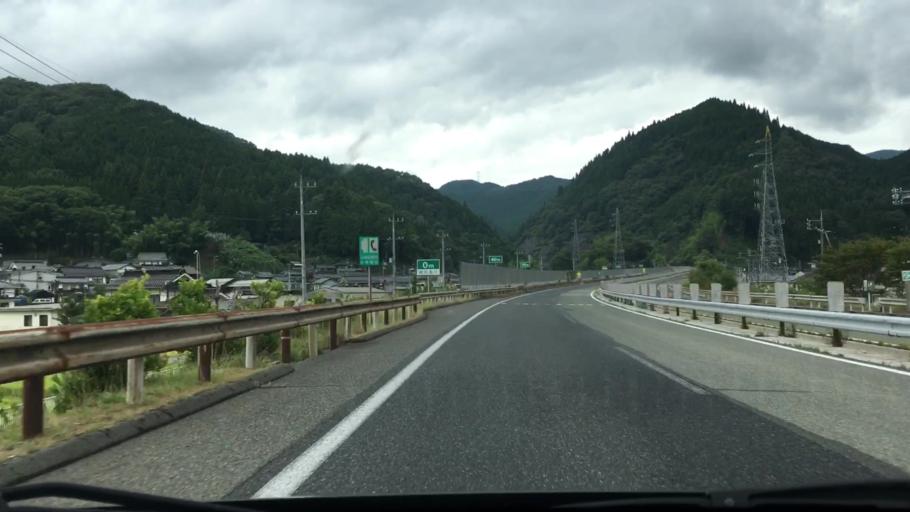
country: JP
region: Okayama
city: Niimi
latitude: 35.0091
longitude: 133.4358
